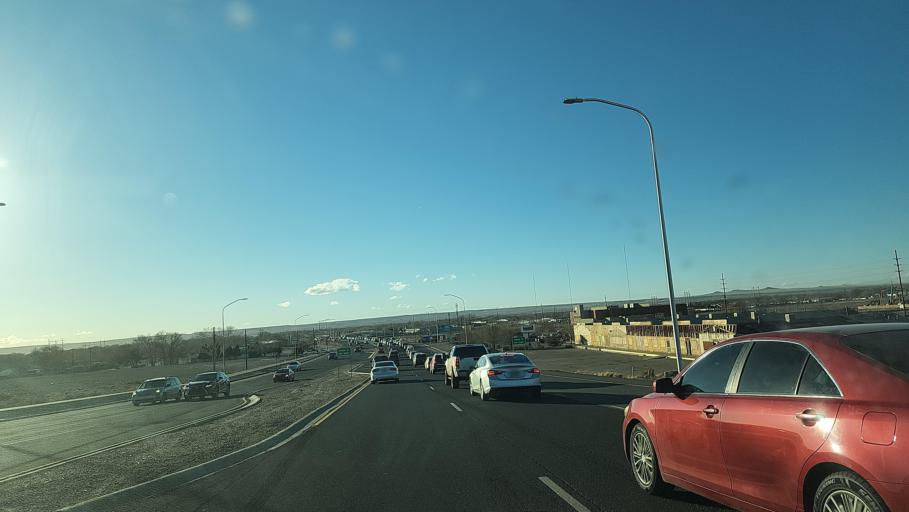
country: US
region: New Mexico
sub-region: Bernalillo County
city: South Valley
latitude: 35.0262
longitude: -106.6498
